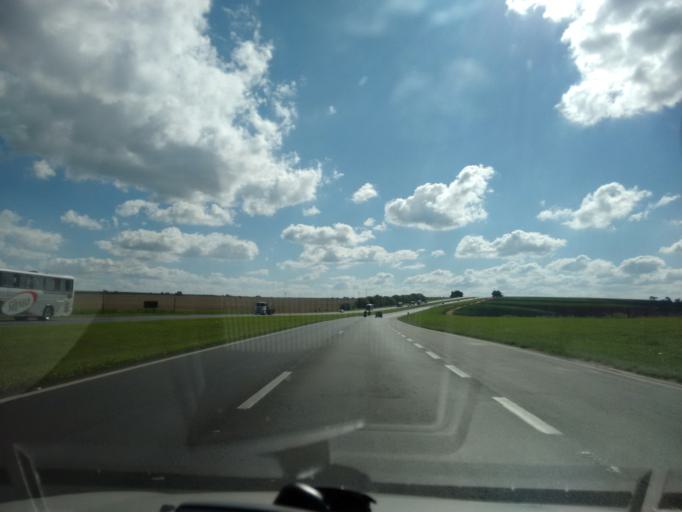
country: BR
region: Sao Paulo
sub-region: Ibate
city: Ibate
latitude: -21.9635
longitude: -47.9734
